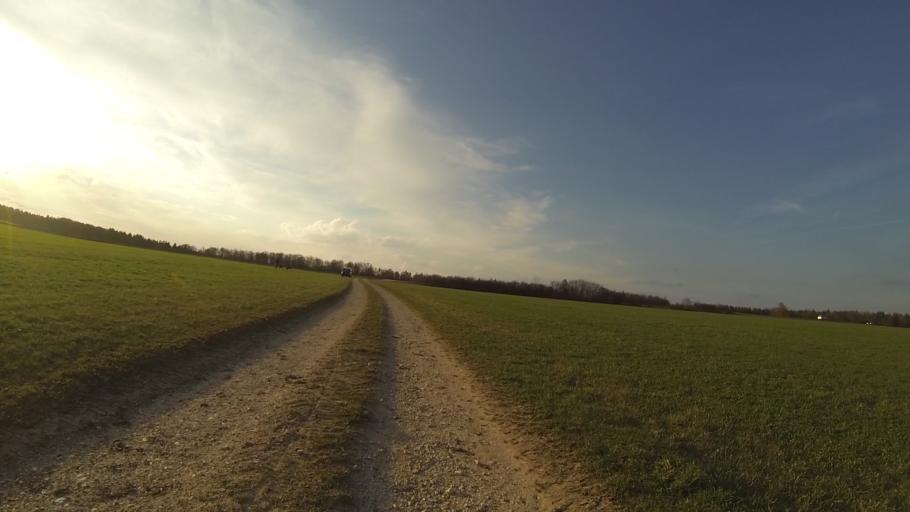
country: DE
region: Baden-Wuerttemberg
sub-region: Regierungsbezirk Stuttgart
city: Heidenheim an der Brenz
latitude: 48.7029
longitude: 10.1332
